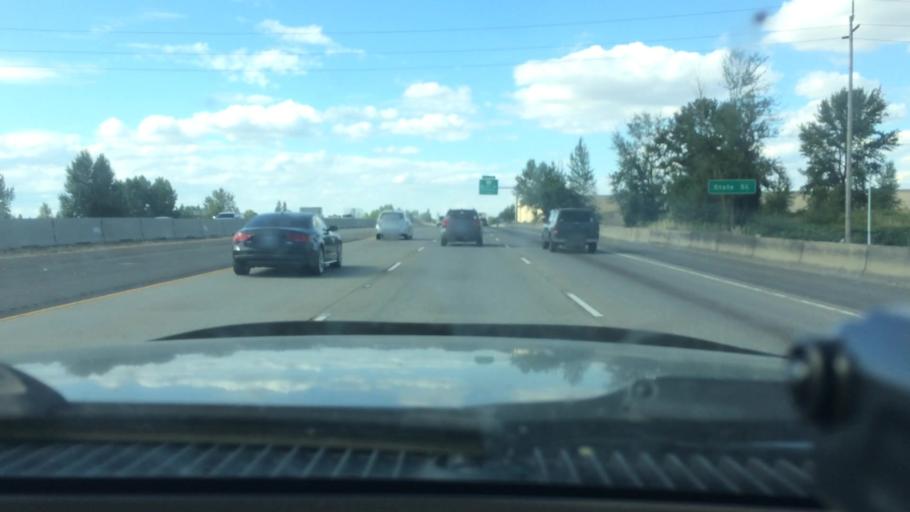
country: US
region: Oregon
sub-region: Marion County
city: Four Corners
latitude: 44.9272
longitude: -122.9902
